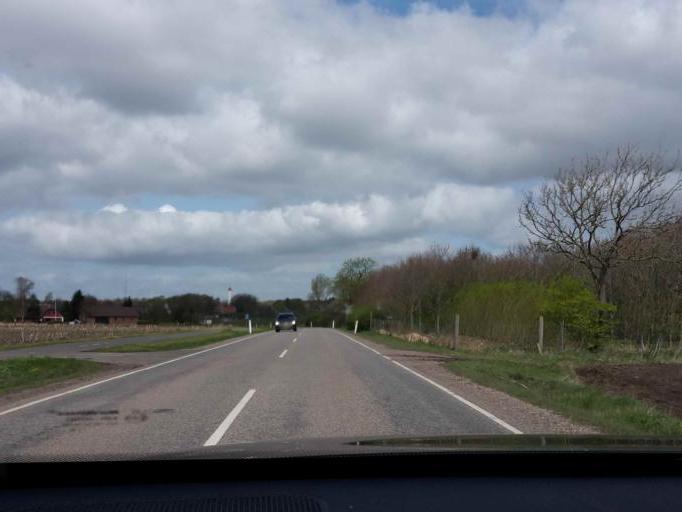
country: DK
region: South Denmark
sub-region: Varde Kommune
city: Olgod
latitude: 55.8005
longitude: 8.6383
